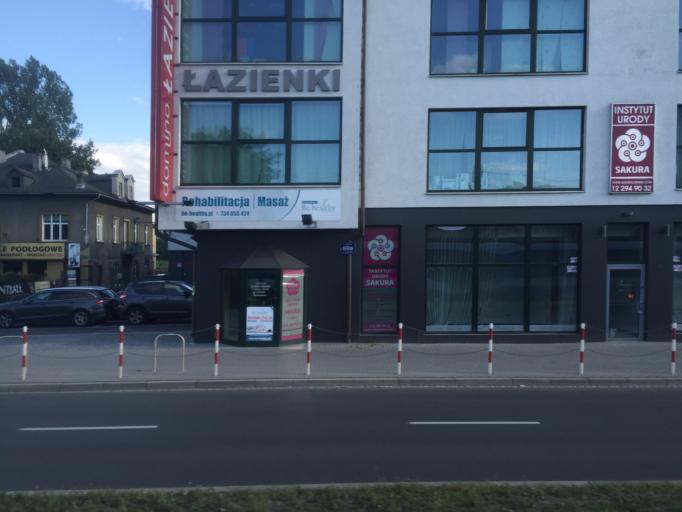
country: PL
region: Lesser Poland Voivodeship
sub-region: Krakow
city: Krakow
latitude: 50.0666
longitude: 19.9712
